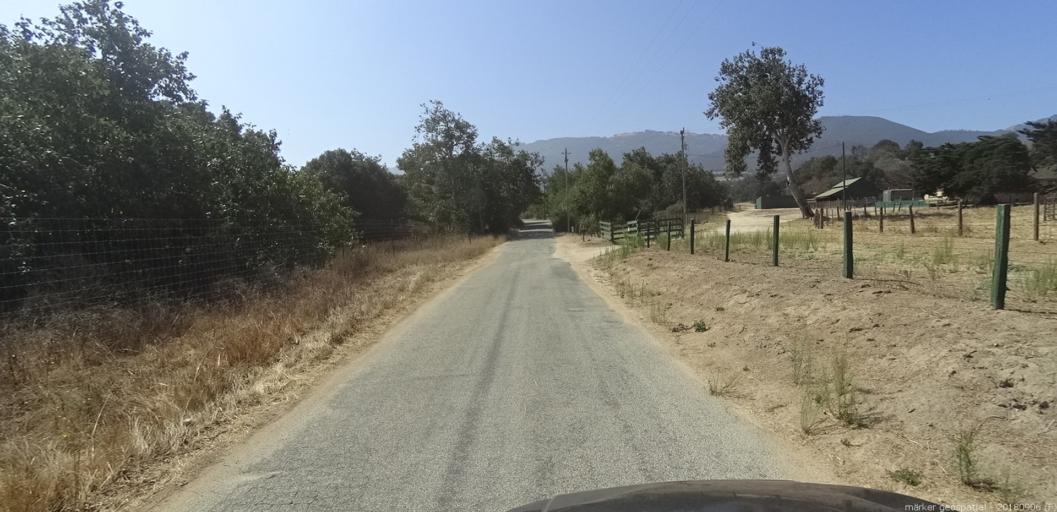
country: US
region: California
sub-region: Monterey County
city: Chualar
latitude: 36.5843
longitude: -121.6071
